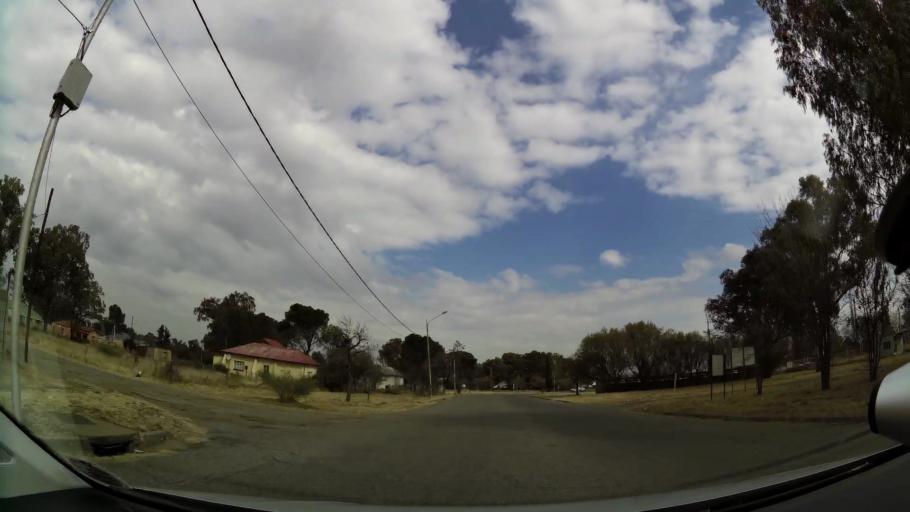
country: ZA
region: Orange Free State
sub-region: Fezile Dabi District Municipality
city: Kroonstad
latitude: -27.6569
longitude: 27.2319
